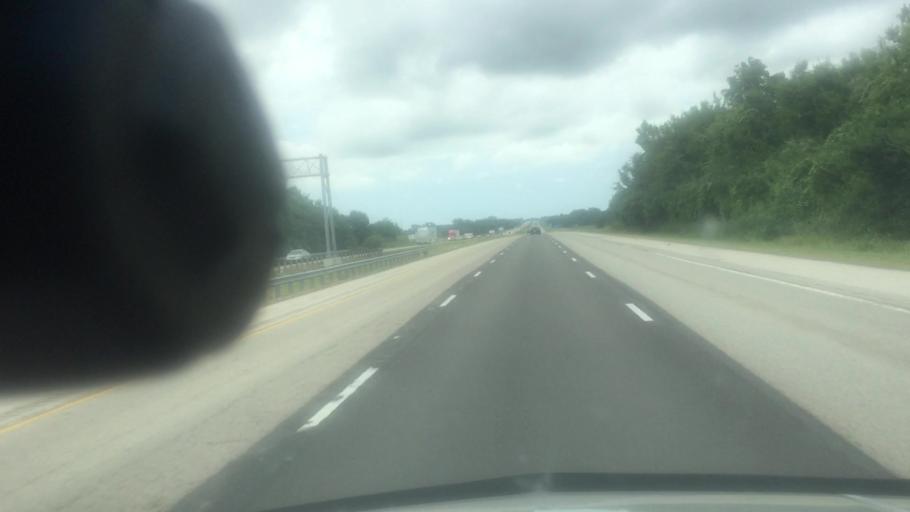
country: US
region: Illinois
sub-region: Logan County
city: Lincoln
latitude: 40.1436
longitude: -89.4174
